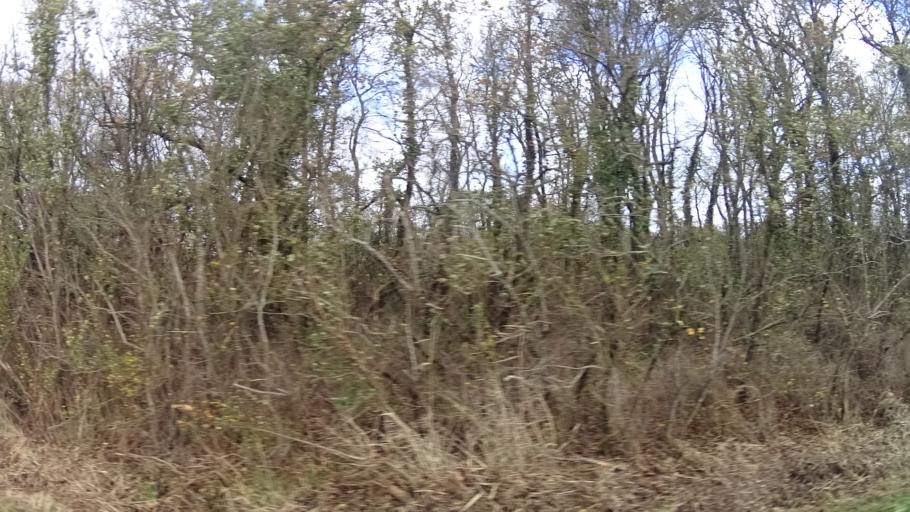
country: FR
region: Brittany
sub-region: Departement du Morbihan
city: Rieux
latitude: 47.5908
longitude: -2.0865
